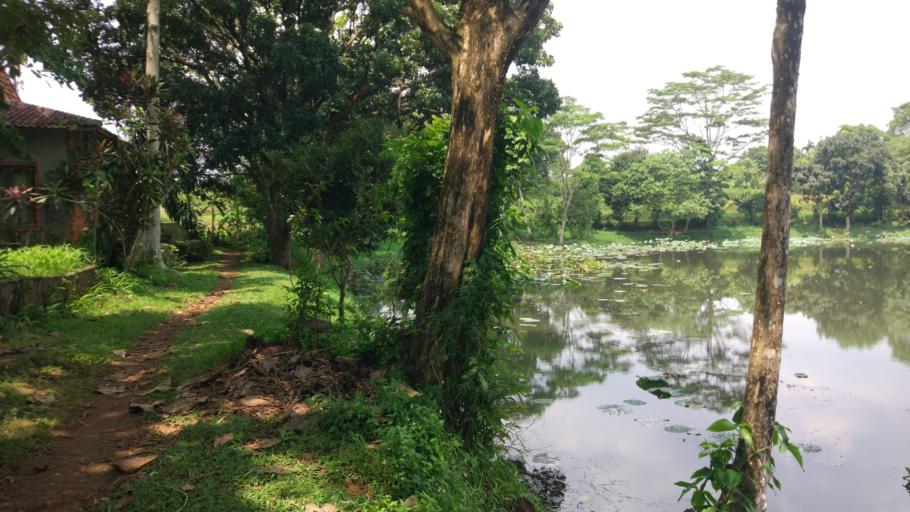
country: ID
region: West Java
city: Ciampea
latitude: -6.5470
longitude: 106.7336
